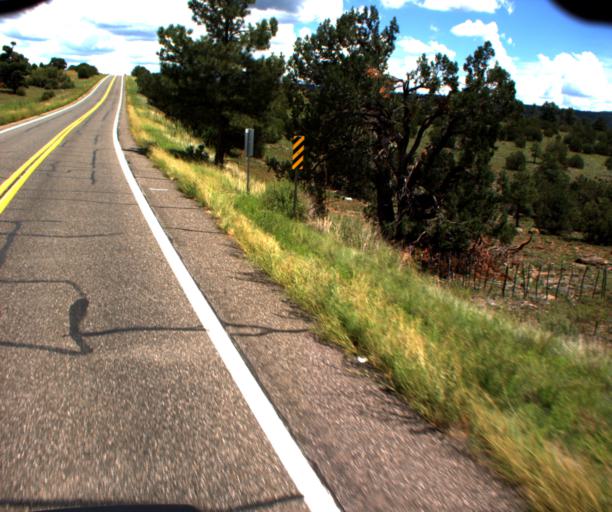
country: US
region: Arizona
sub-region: Gila County
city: Pine
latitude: 34.5140
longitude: -111.5381
